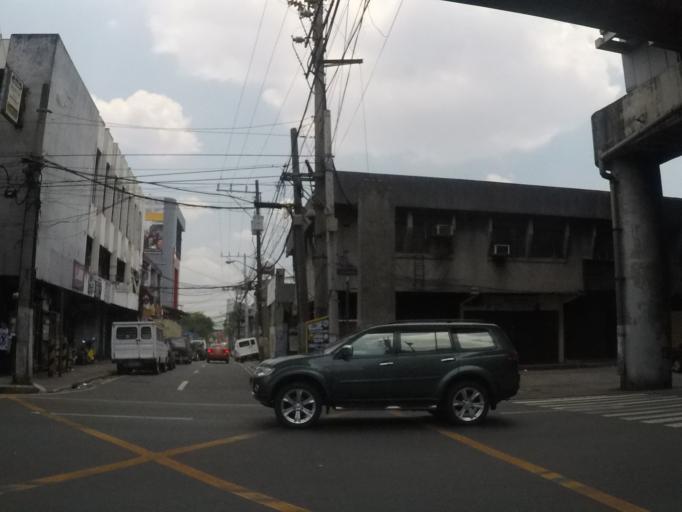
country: PH
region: Metro Manila
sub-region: San Juan
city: San Juan
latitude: 14.6103
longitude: 121.0257
